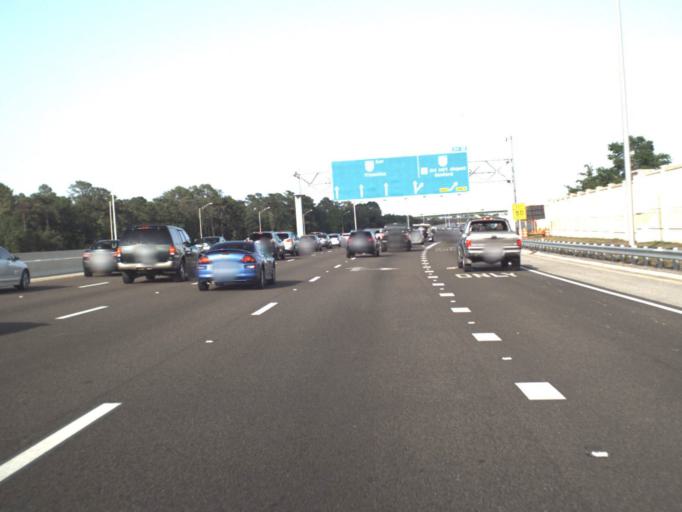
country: US
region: Florida
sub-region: Orange County
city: Union Park
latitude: 28.5468
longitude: -81.2715
